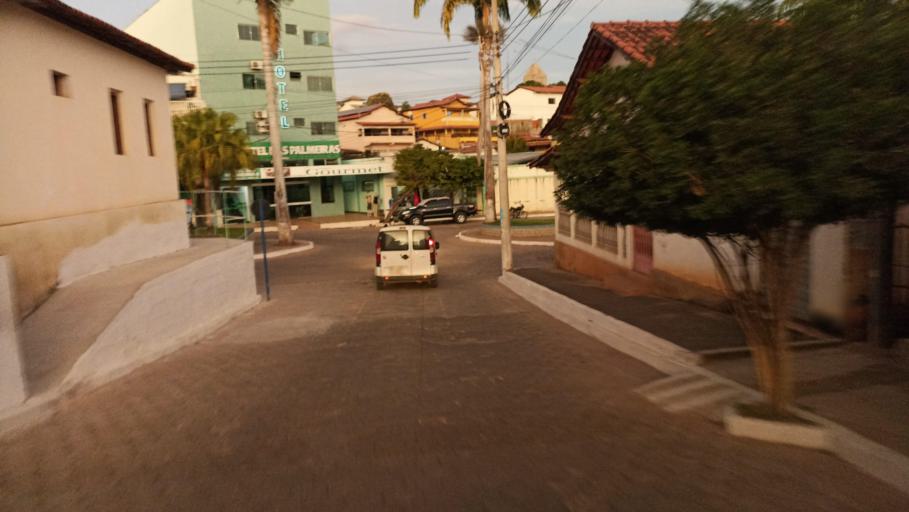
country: BR
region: Minas Gerais
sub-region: Aracuai
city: Aracuai
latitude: -16.6181
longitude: -42.1831
